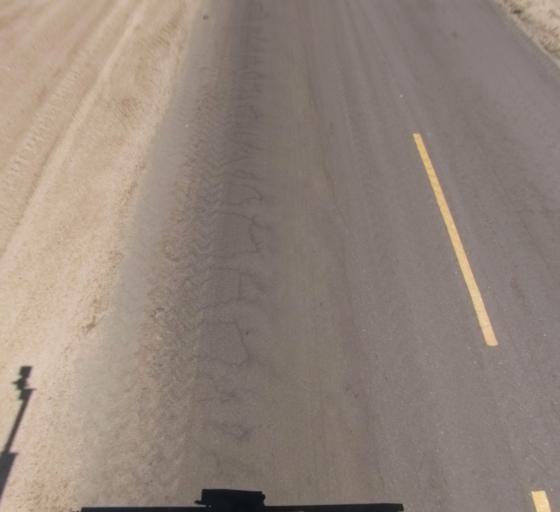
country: US
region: California
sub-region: Madera County
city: Parksdale
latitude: 36.8782
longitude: -119.9469
